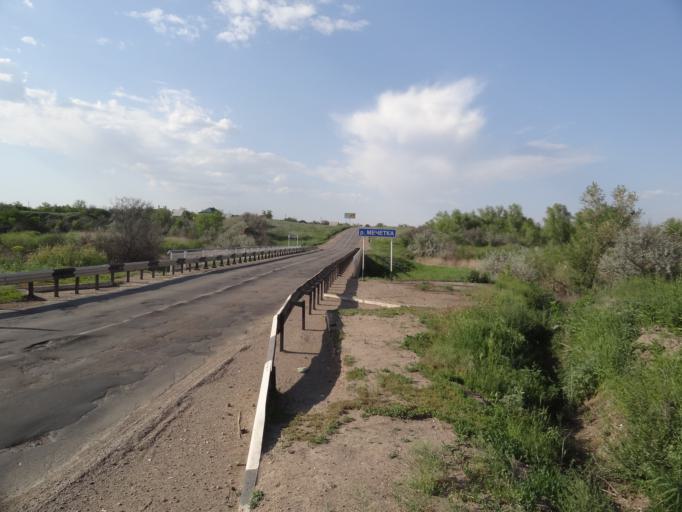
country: RU
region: Saratov
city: Privolzhskiy
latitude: 51.3483
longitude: 46.0444
